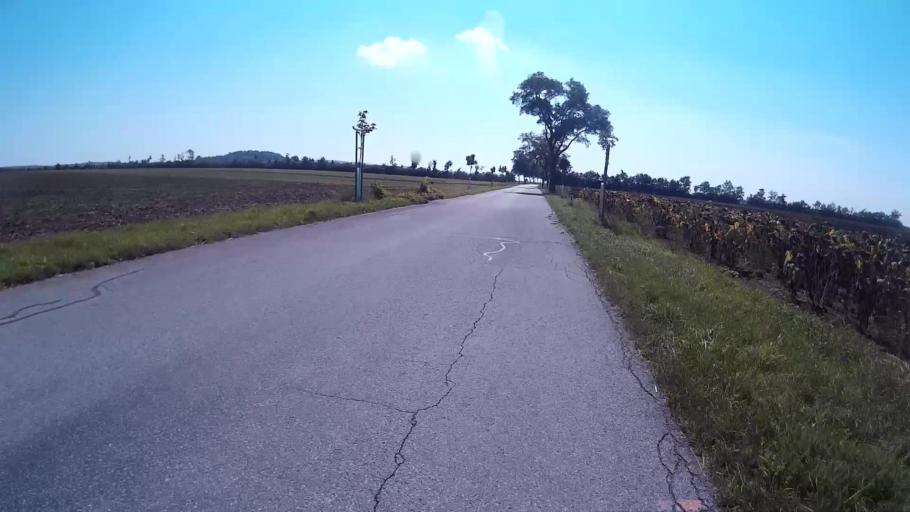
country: CZ
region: South Moravian
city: Novosedly
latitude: 48.7807
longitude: 16.4931
